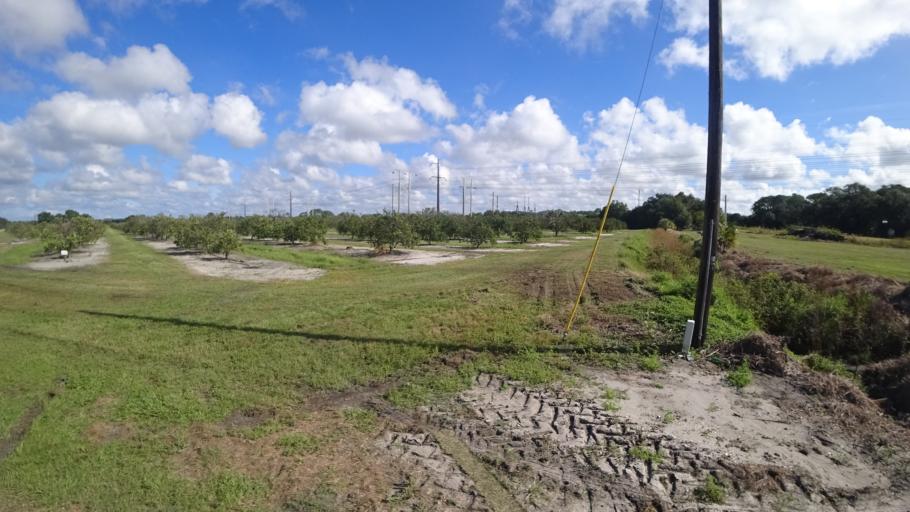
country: US
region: Florida
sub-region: Manatee County
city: Ellenton
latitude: 27.5793
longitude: -82.4601
